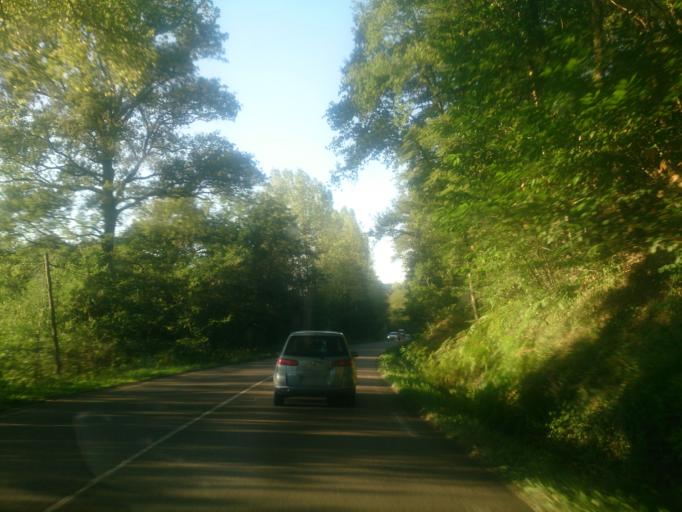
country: FR
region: Limousin
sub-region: Departement de la Correze
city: Brive-la-Gaillarde
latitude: 45.1310
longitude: 1.5170
